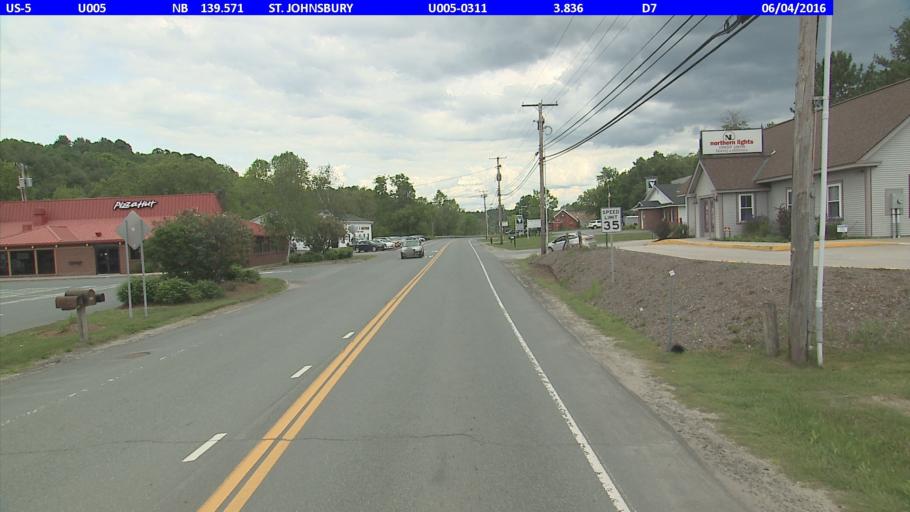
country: US
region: Vermont
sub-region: Caledonia County
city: St Johnsbury
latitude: 44.4466
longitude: -72.0157
